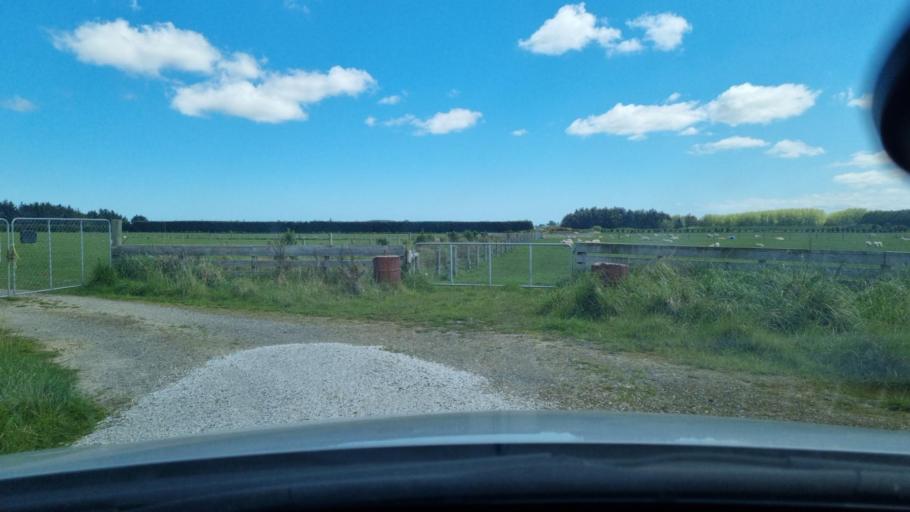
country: NZ
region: Southland
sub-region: Invercargill City
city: Invercargill
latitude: -46.3740
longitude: 168.3377
